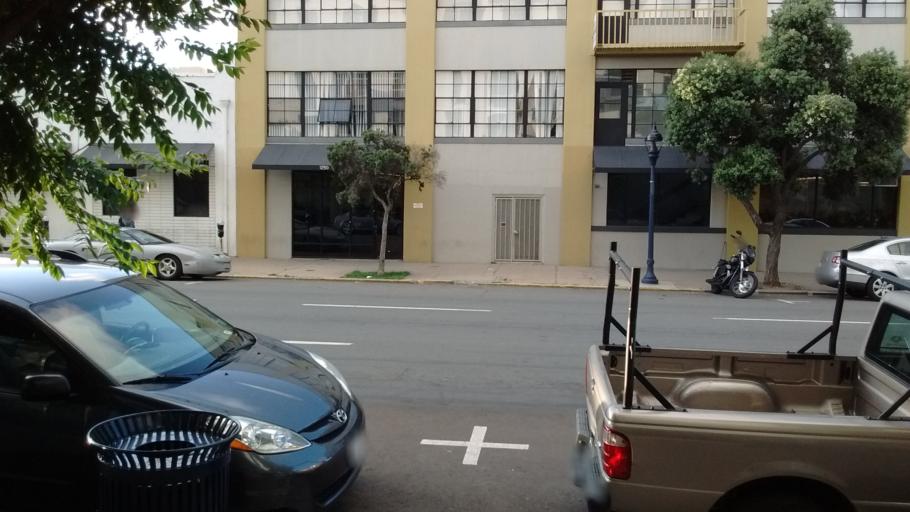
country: US
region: California
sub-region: San Diego County
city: San Diego
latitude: 32.7127
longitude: -117.1532
